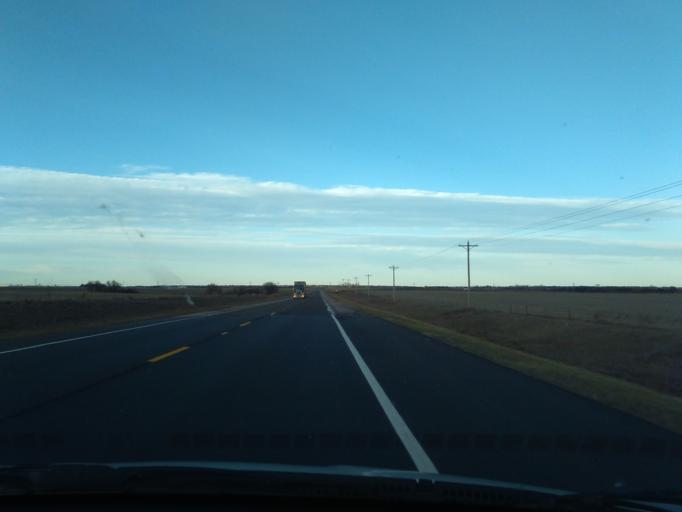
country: US
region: Nebraska
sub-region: Phelps County
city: Holdrege
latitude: 40.3827
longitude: -99.3701
